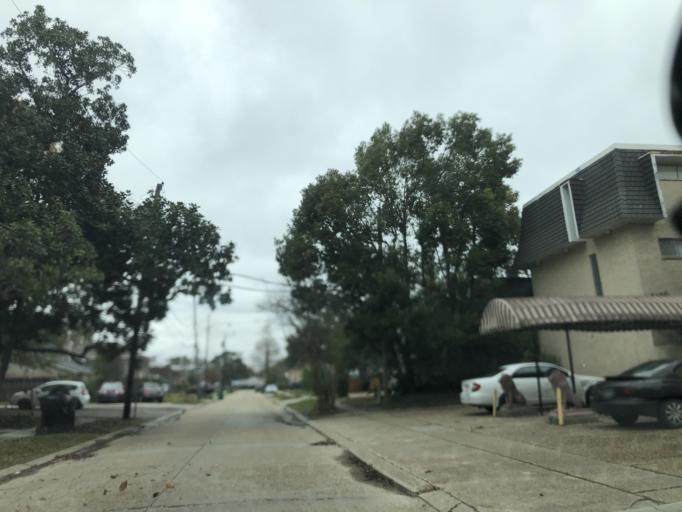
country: US
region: Louisiana
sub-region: Jefferson Parish
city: Metairie Terrace
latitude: 29.9764
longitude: -90.1585
